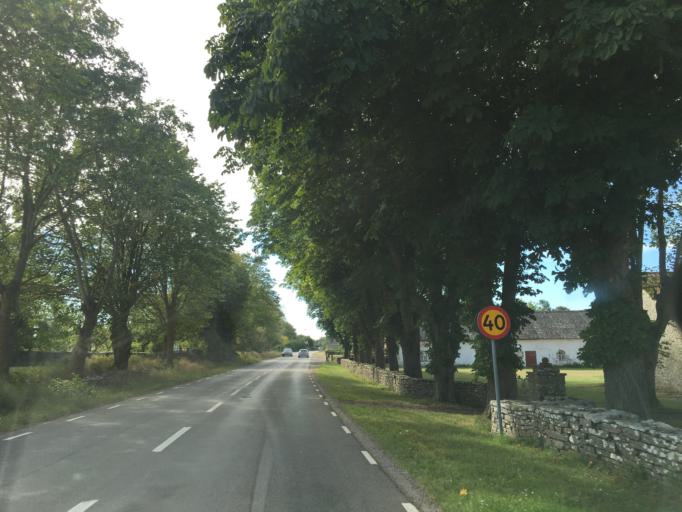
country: SE
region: Kalmar
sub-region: Morbylanga Kommun
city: Moerbylanga
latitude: 56.4631
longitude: 16.4302
